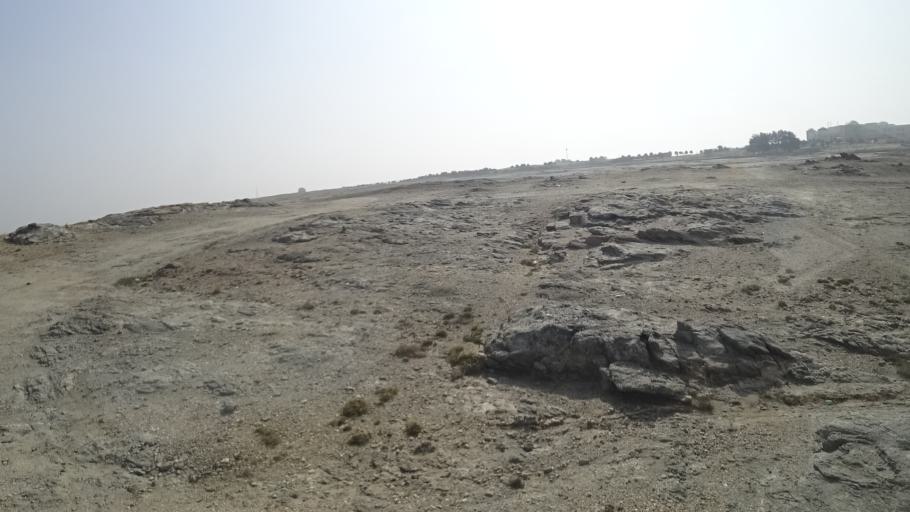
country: OM
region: Zufar
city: Salalah
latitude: 16.9595
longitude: 54.7331
